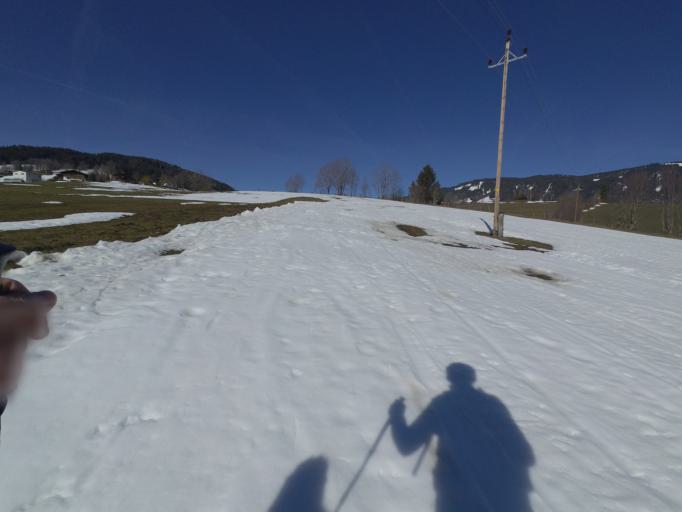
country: AT
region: Salzburg
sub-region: Politischer Bezirk Sankt Johann im Pongau
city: Goldegg
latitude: 47.3155
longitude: 13.0822
